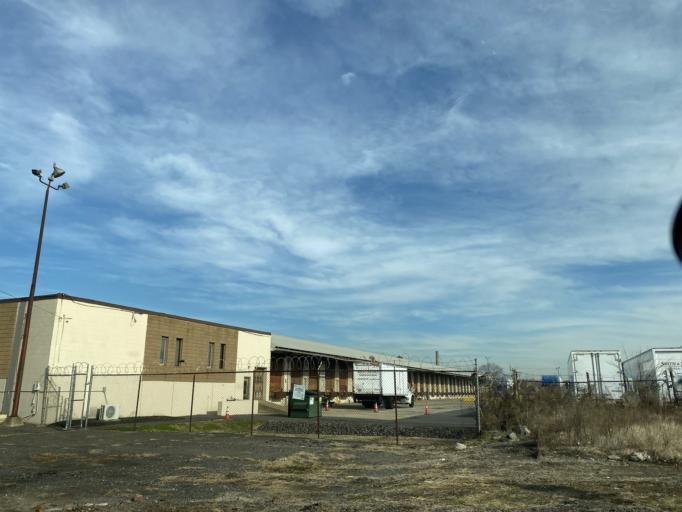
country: US
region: New Jersey
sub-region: Camden County
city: Pennsauken
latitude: 40.0049
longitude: -75.0854
